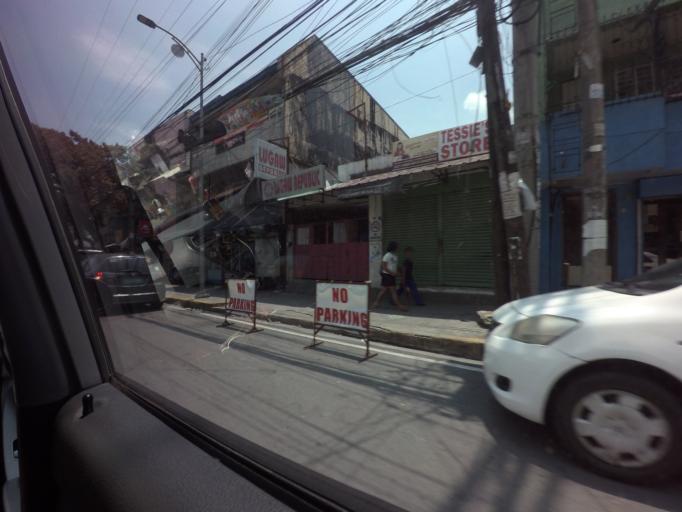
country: PH
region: Metro Manila
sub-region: City of Manila
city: Quiapo
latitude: 14.5844
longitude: 120.9992
